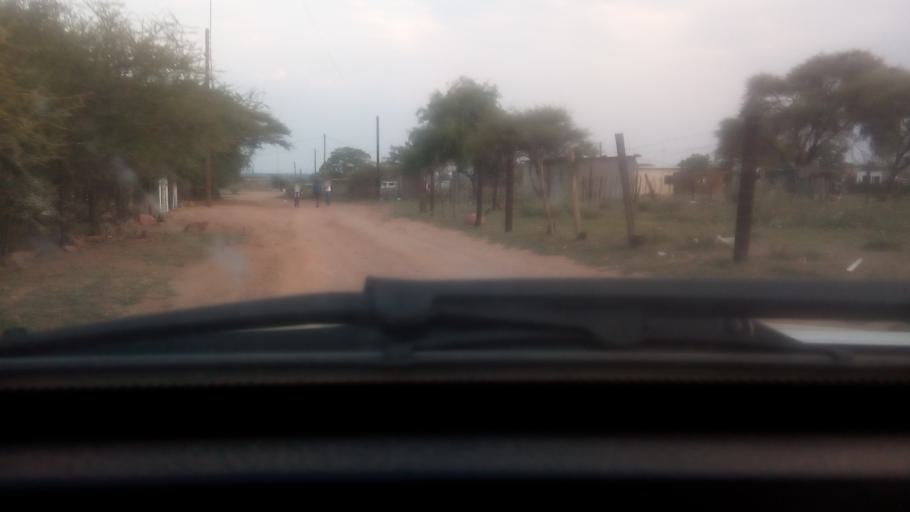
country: BW
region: Kgatleng
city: Bokaa
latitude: -24.4271
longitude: 26.0204
